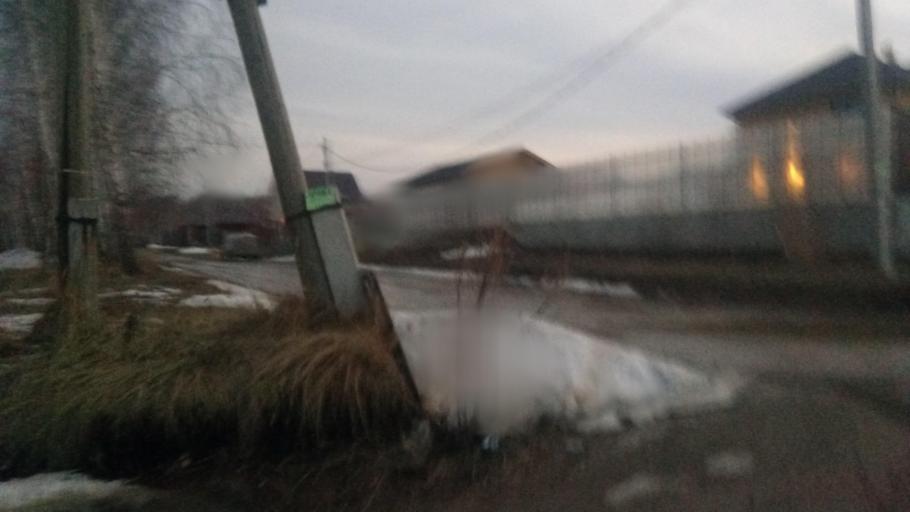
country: RU
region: Chelyabinsk
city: Sargazy
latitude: 55.1036
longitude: 61.2025
